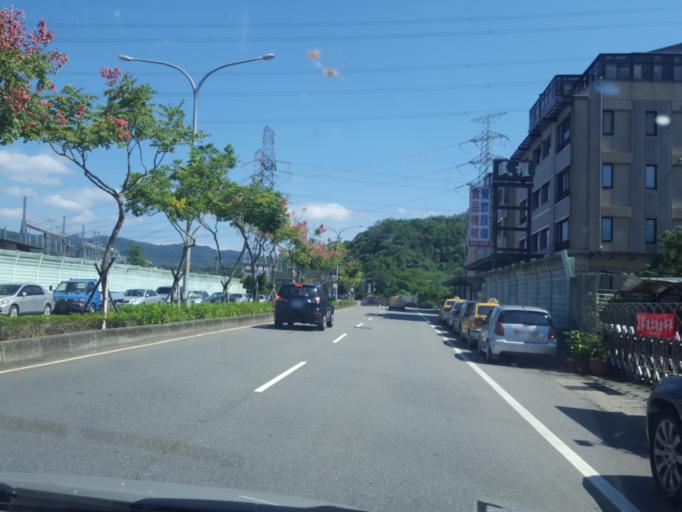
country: TW
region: Taipei
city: Taipei
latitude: 25.0002
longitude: 121.6220
